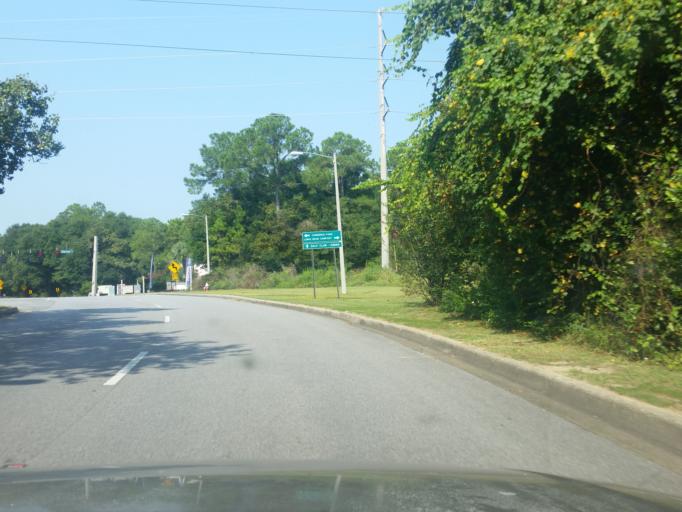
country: US
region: Florida
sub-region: Escambia County
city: Brent
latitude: 30.4803
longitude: -87.2656
